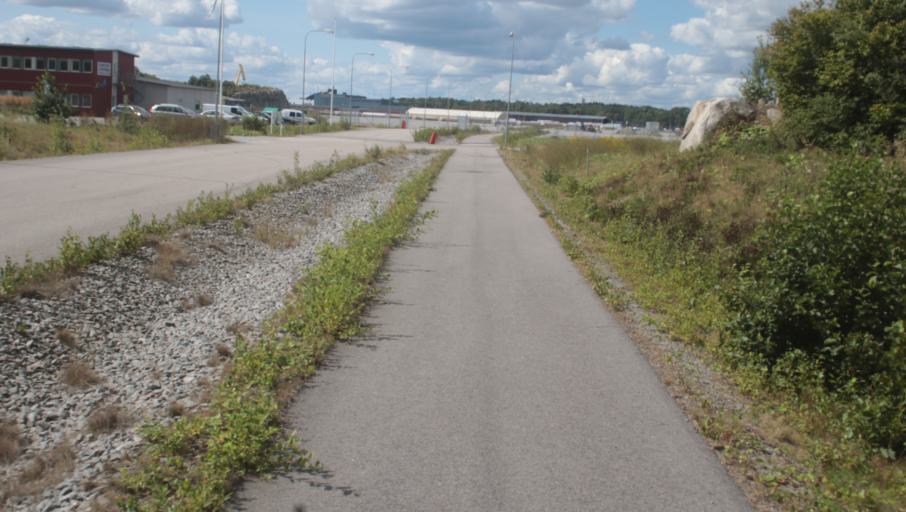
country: SE
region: Blekinge
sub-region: Karlshamns Kommun
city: Karlshamn
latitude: 56.1626
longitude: 14.8379
